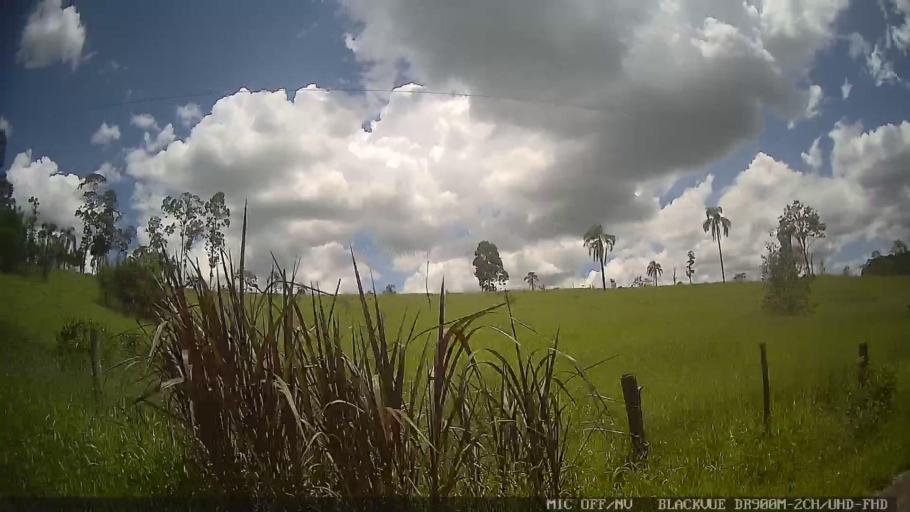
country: BR
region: Sao Paulo
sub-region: Braganca Paulista
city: Braganca Paulista
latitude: -22.9991
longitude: -46.4519
